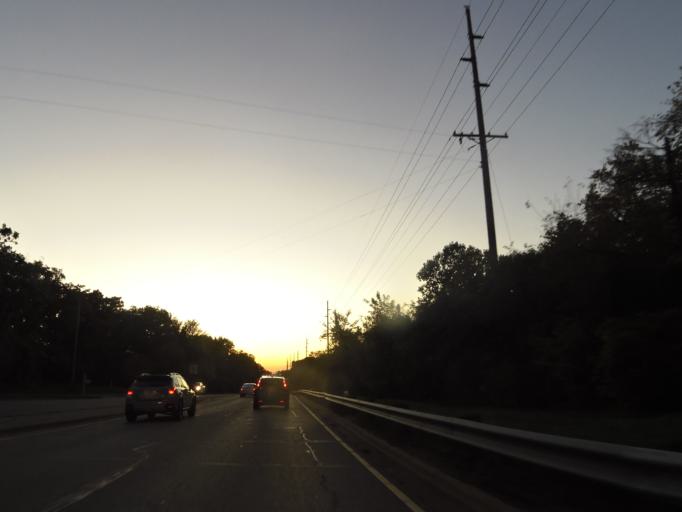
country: US
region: Minnesota
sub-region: Dakota County
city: Eagan
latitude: 44.7901
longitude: -93.1898
